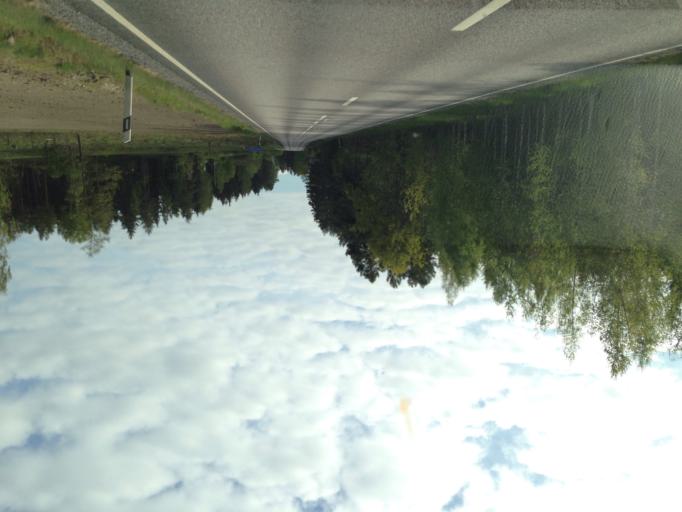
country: SE
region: Soedermanland
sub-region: Flens Kommun
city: Malmkoping
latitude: 59.0211
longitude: 16.8488
